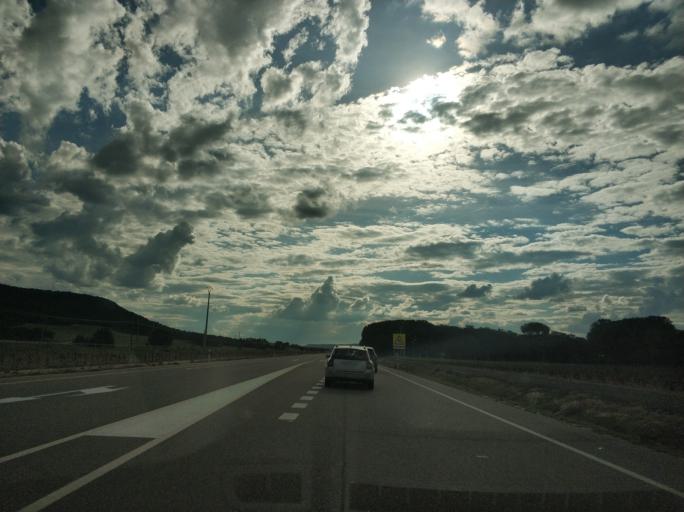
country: ES
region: Castille and Leon
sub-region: Provincia de Valladolid
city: Valbuena de Duero
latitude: 41.6277
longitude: -4.3258
